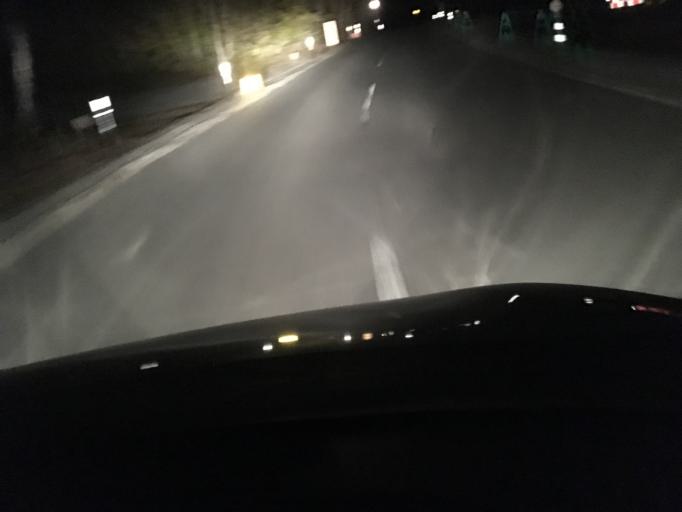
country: JP
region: Miyagi
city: Furukawa
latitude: 38.8639
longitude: 140.7747
